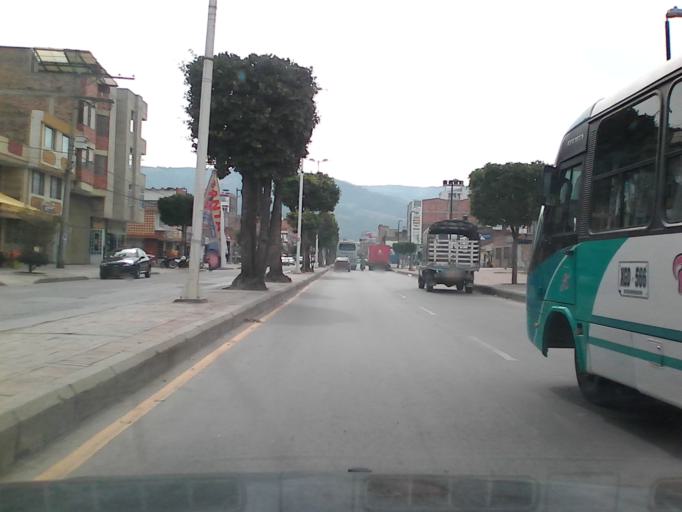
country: CO
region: Boyaca
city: Sogamoso
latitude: 5.7213
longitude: -72.9392
